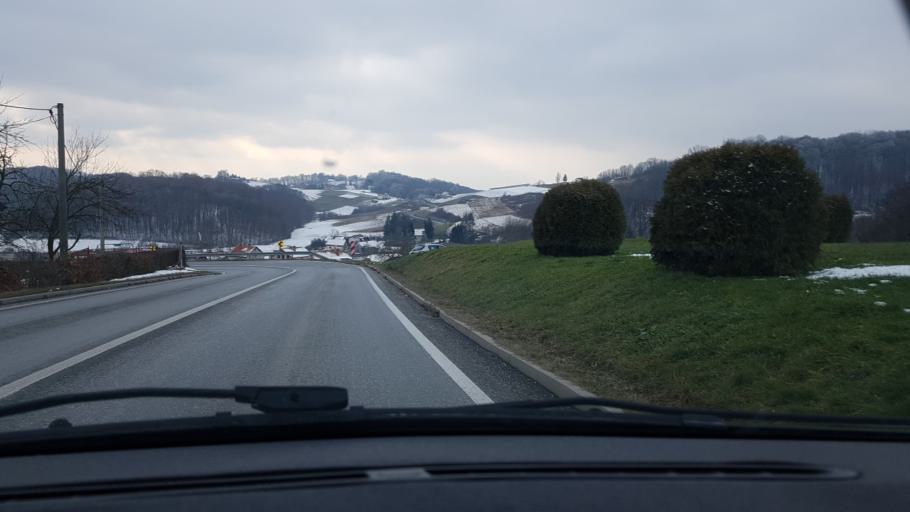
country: HR
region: Krapinsko-Zagorska
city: Mihovljan
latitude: 46.1540
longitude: 15.9633
